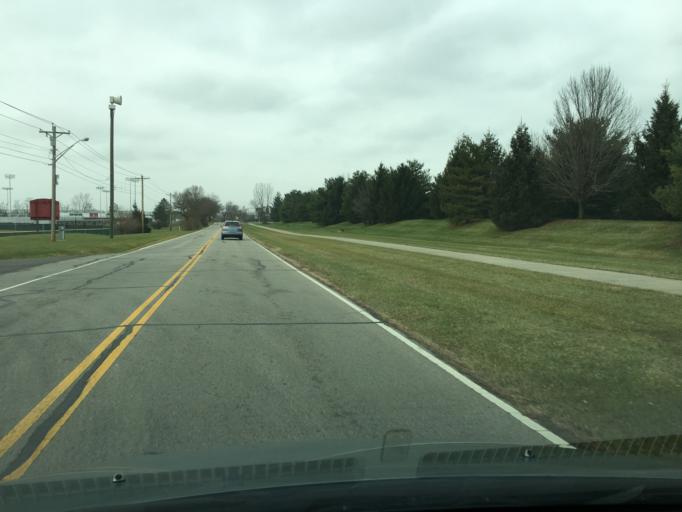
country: US
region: Ohio
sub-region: Butler County
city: Beckett Ridge
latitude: 39.3316
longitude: -84.4289
